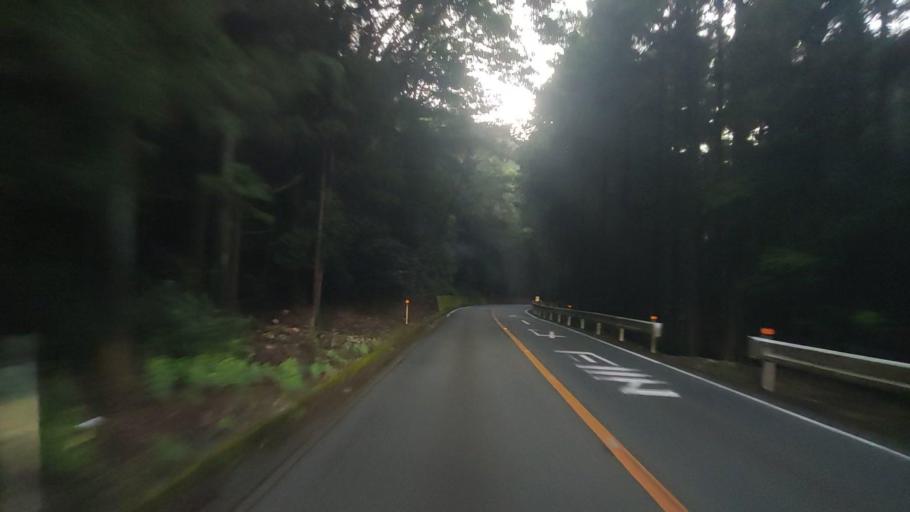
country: JP
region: Mie
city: Ise
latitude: 34.4458
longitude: 136.7511
